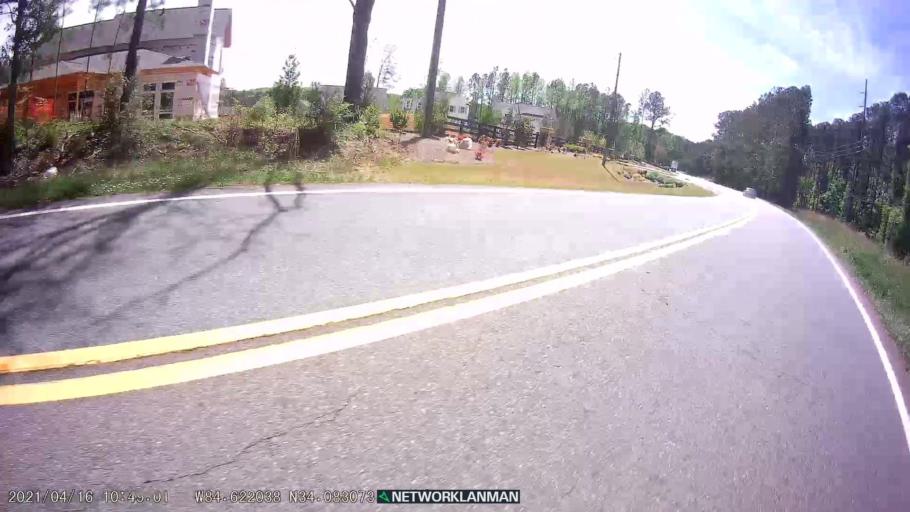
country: US
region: Georgia
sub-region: Cobb County
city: Acworth
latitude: 34.0828
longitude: -84.6224
